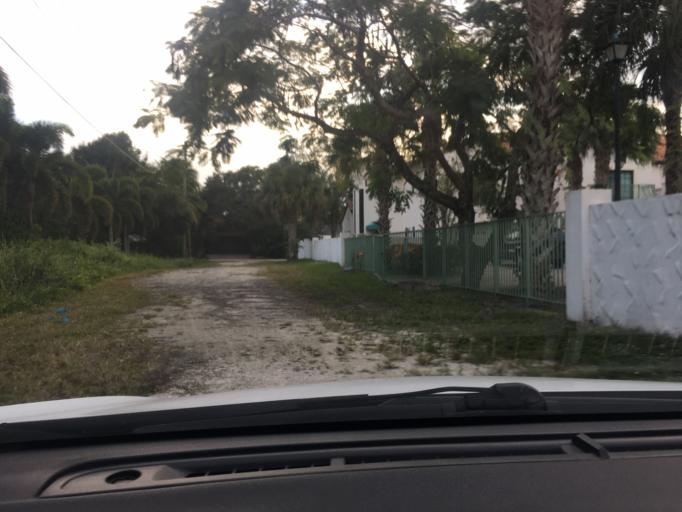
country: US
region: Florida
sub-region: Broward County
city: Dania Beach
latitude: 26.0668
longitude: -80.1801
